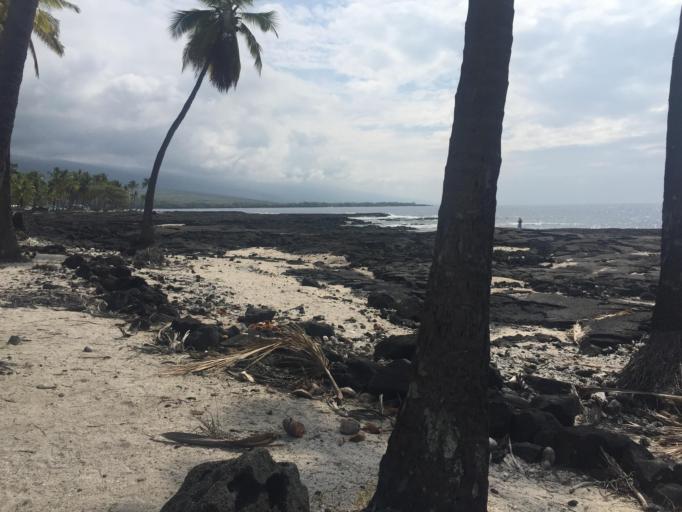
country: US
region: Hawaii
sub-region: Hawaii County
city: Honaunau-Napoopoo
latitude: 19.4199
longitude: -155.9130
